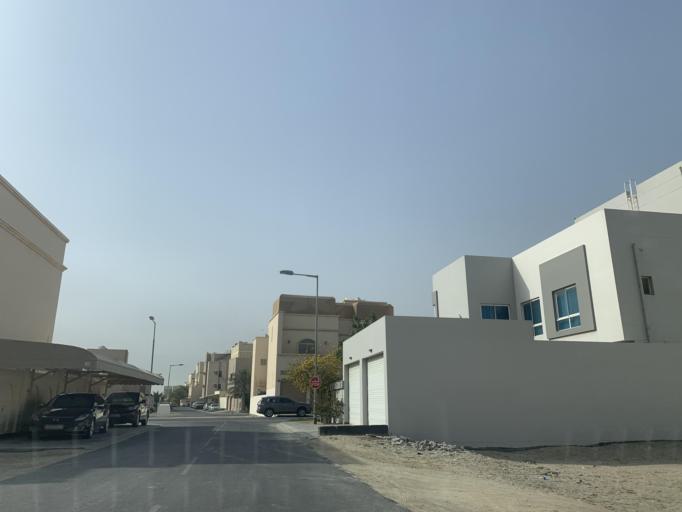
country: BH
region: Northern
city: Madinat `Isa
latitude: 26.1882
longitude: 50.5632
